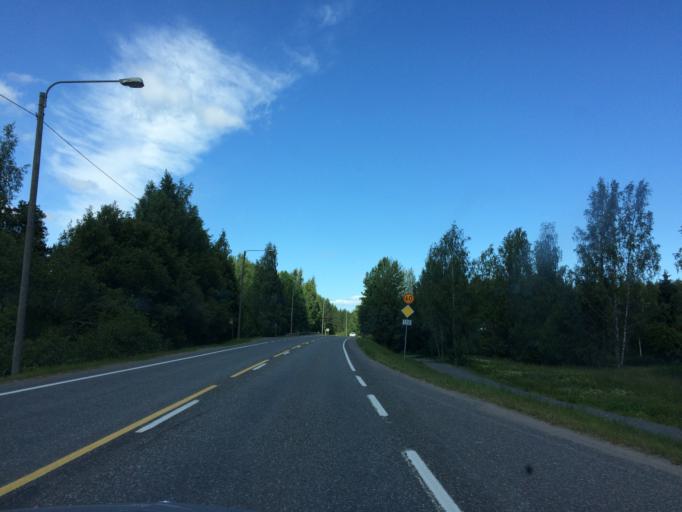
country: FI
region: Haeme
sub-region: Haemeenlinna
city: Haemeenlinna
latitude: 60.9607
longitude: 24.4840
